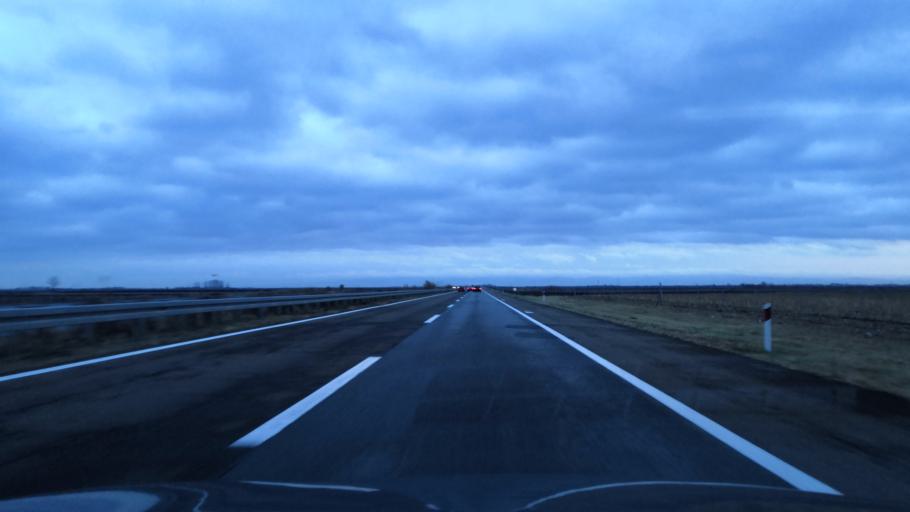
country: RS
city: Kisac
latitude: 45.3951
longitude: 19.7412
